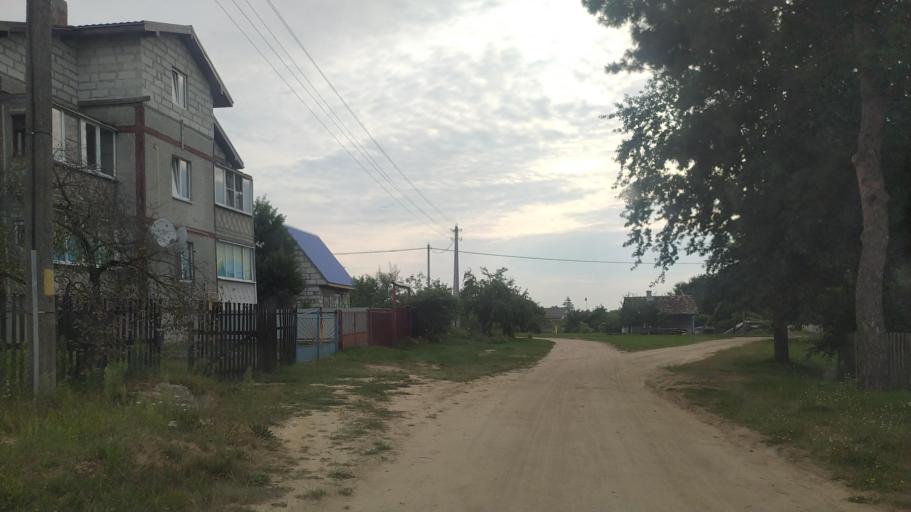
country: BY
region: Brest
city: Byaroza
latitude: 52.5541
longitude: 24.9695
